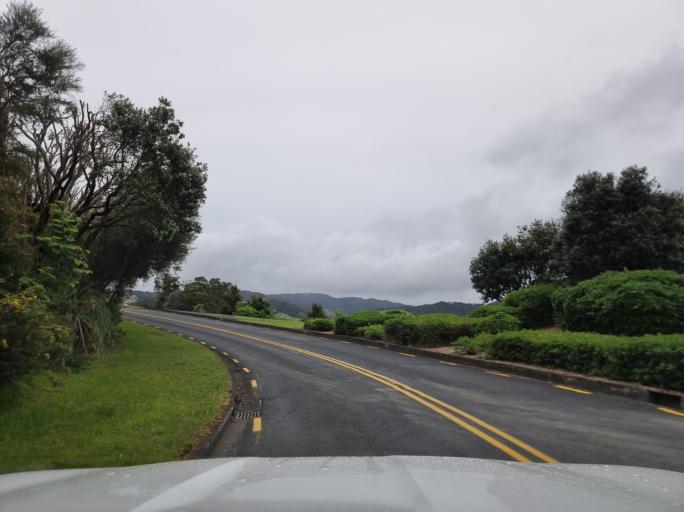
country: NZ
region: Northland
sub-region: Whangarei
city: Whangarei
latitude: -35.7685
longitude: 174.3706
